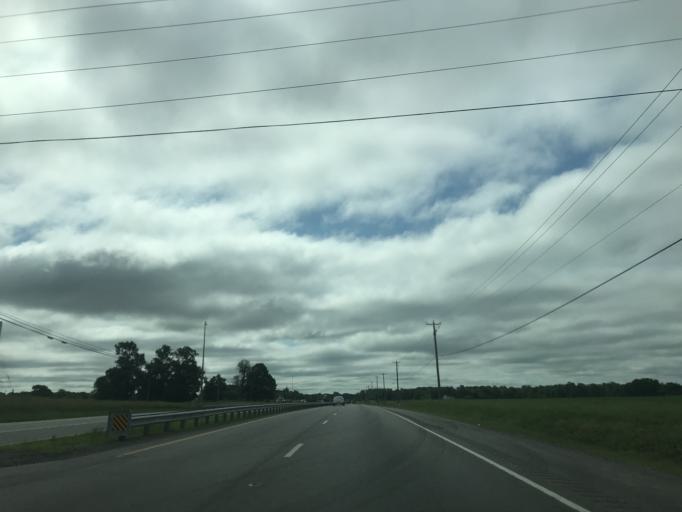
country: US
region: Maryland
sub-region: Queen Anne's County
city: Grasonville
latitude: 38.9727
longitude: -76.1241
